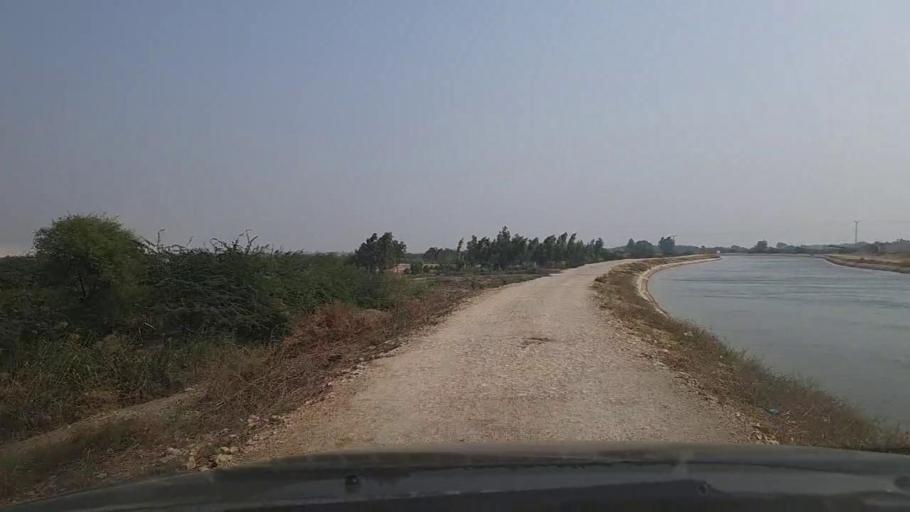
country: PK
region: Sindh
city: Thatta
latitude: 24.8028
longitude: 67.9036
